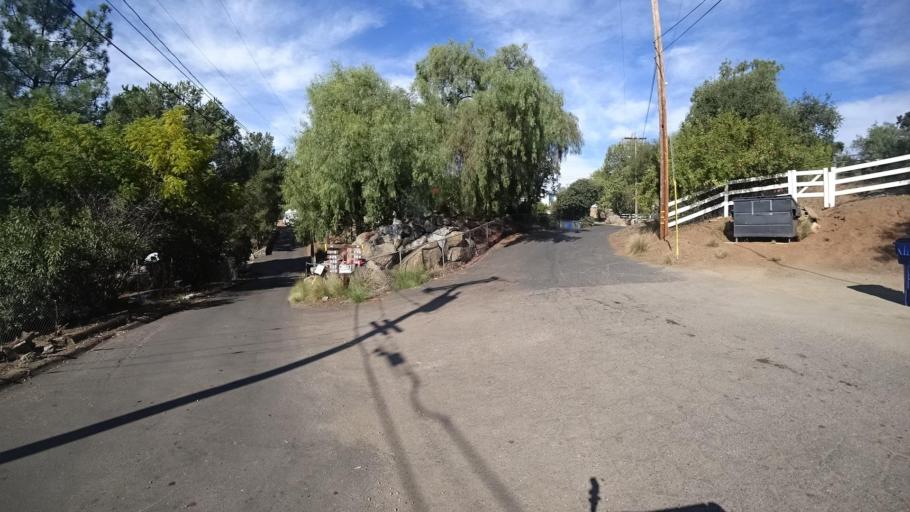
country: US
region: California
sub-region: San Diego County
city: Harbison Canyon
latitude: 32.8190
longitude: -116.8070
